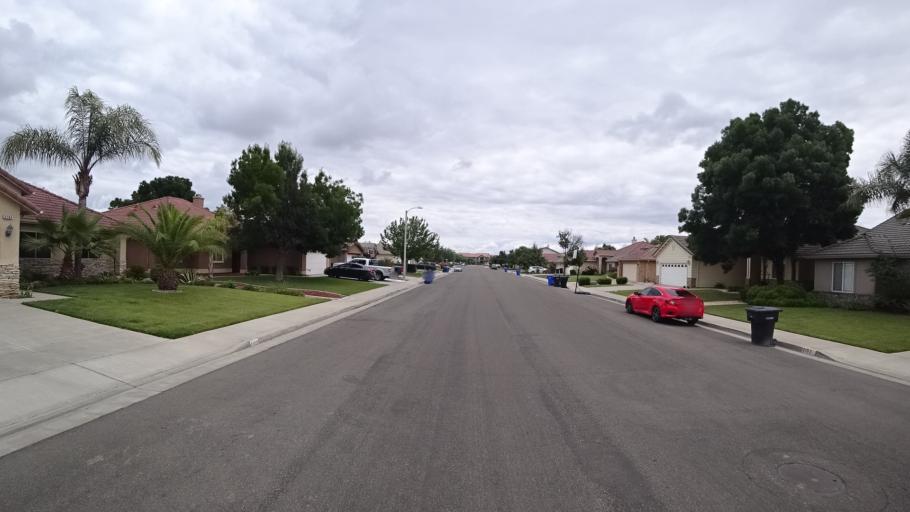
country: US
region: California
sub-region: Kings County
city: Armona
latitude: 36.3310
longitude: -119.6819
